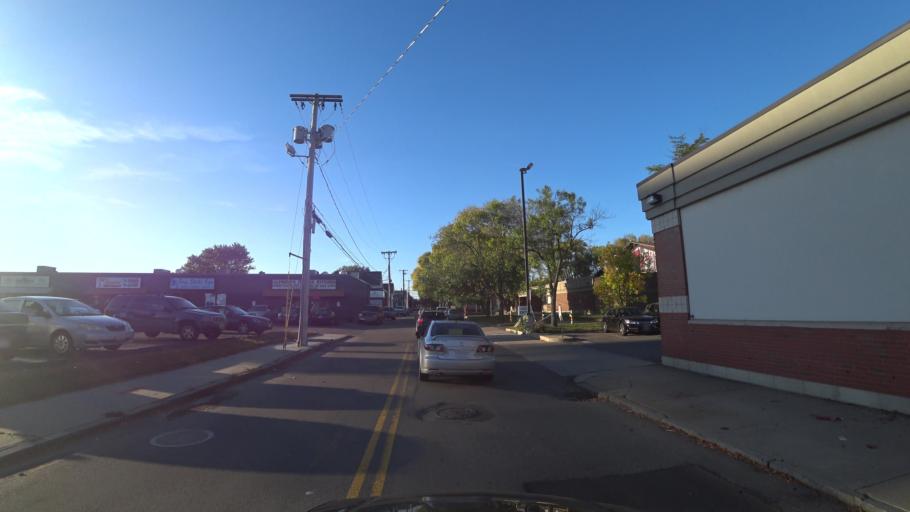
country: US
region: Massachusetts
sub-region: Essex County
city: Lynn
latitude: 42.4566
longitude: -70.9531
